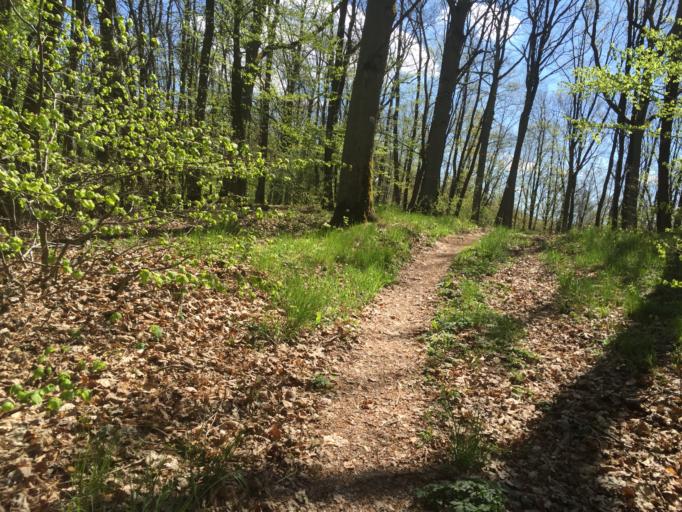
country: DE
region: Bavaria
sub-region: Regierungsbezirk Unterfranken
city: Sulzfeld
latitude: 50.2648
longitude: 10.4340
